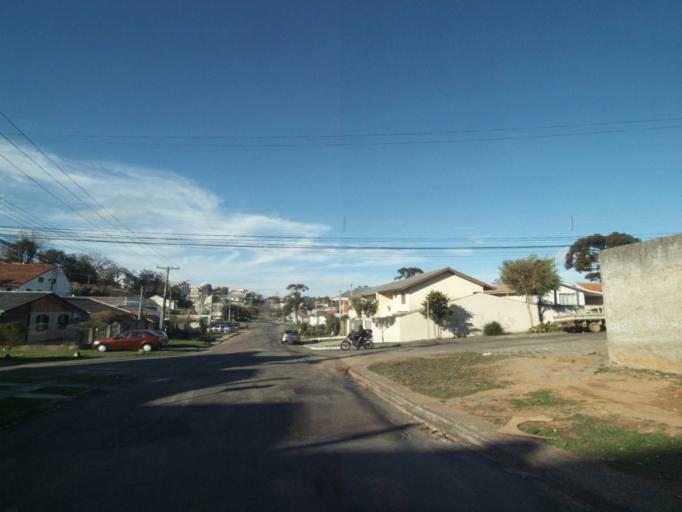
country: BR
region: Parana
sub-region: Curitiba
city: Curitiba
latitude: -25.3864
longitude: -49.2526
